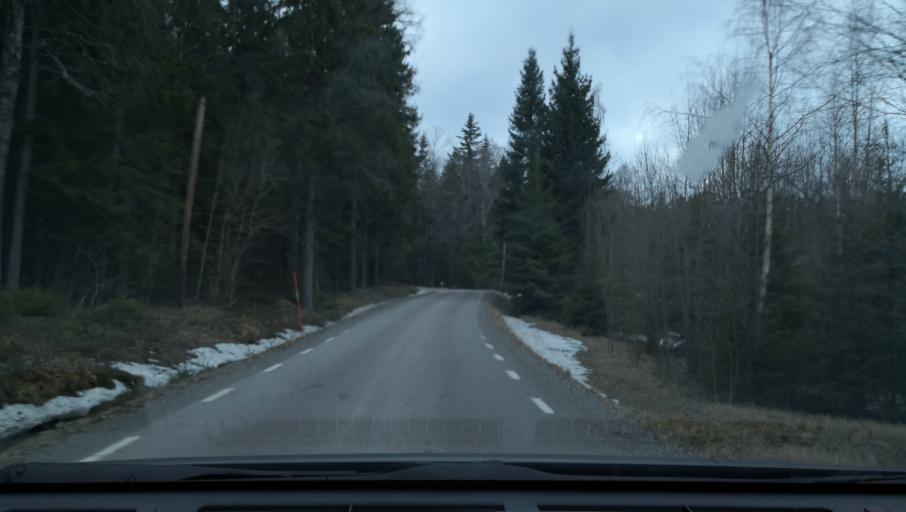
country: SE
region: Vaestmanland
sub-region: Kopings Kommun
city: Kolsva
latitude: 59.5698
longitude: 15.7255
